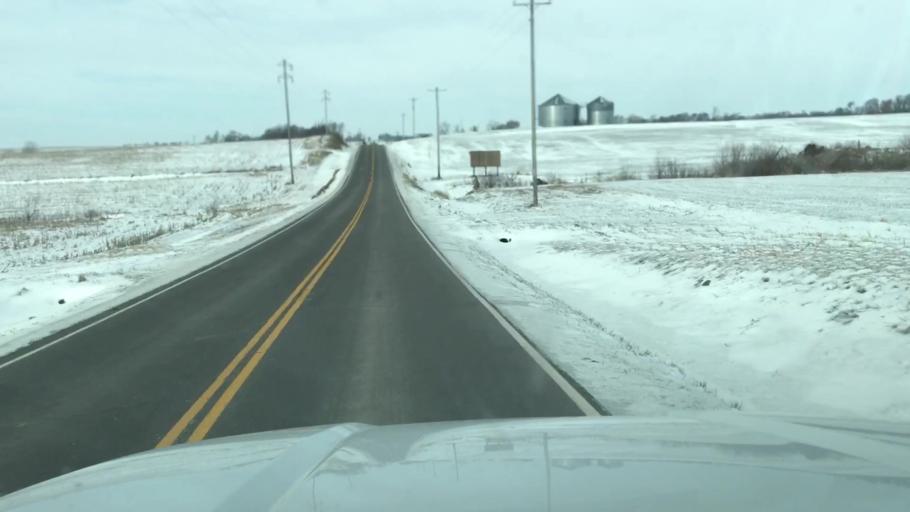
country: US
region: Missouri
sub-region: Holt County
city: Mound City
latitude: 40.1301
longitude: -95.0967
